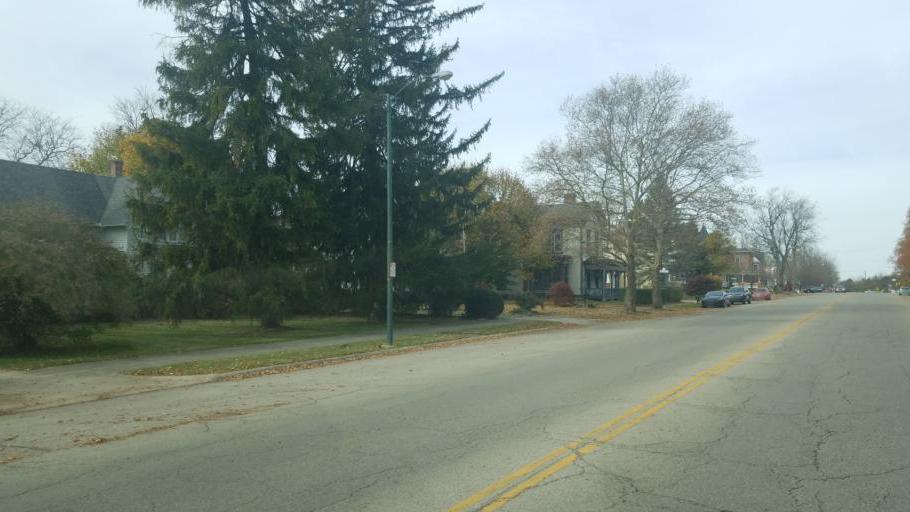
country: US
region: Ohio
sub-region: Madison County
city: London
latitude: 39.8892
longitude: -83.4517
